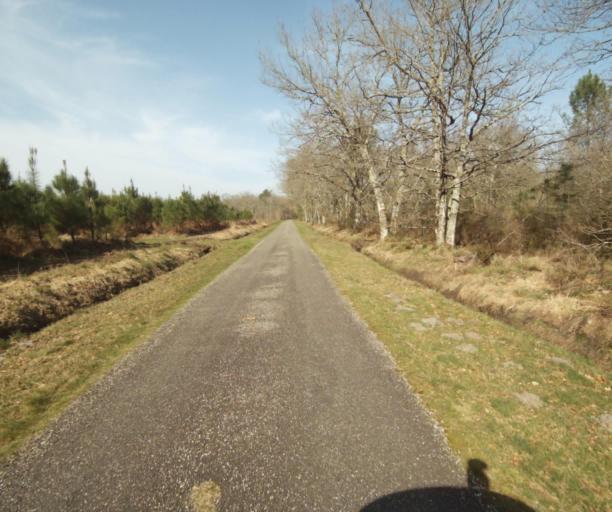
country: FR
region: Aquitaine
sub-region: Departement des Landes
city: Roquefort
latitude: 44.1474
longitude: -0.2056
